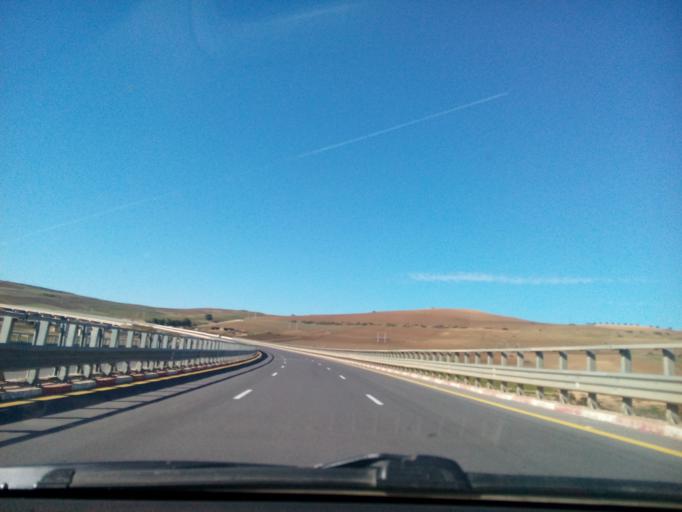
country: DZ
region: Tlemcen
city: Sidi Abdelli
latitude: 35.0402
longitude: -1.0632
